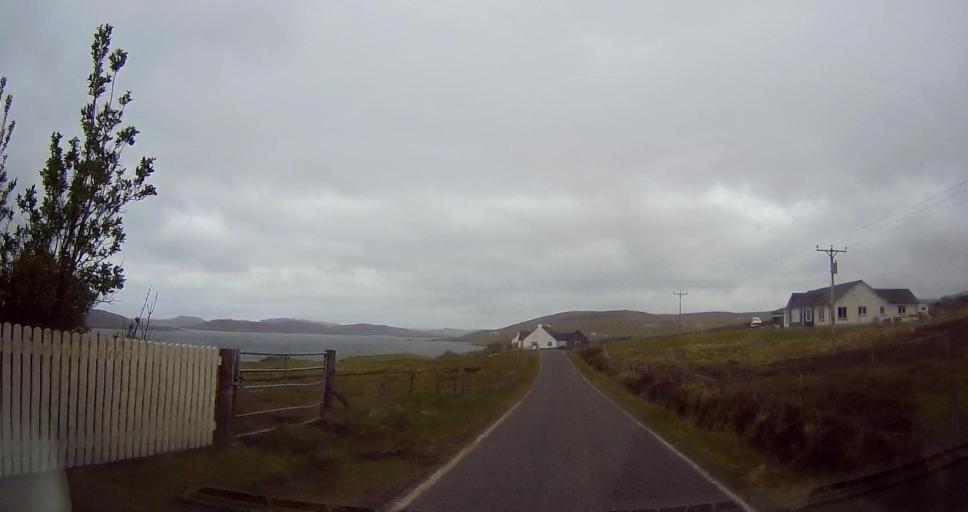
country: GB
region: Scotland
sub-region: Shetland Islands
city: Lerwick
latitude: 60.2951
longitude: -1.3639
